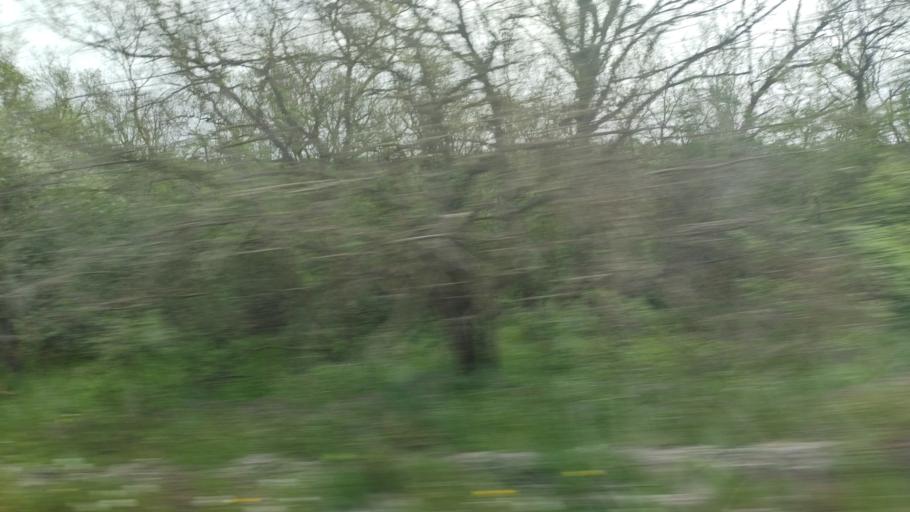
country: RO
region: Constanta
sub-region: Oras Murfatlar
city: Murfatlar
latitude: 44.1641
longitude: 28.3897
